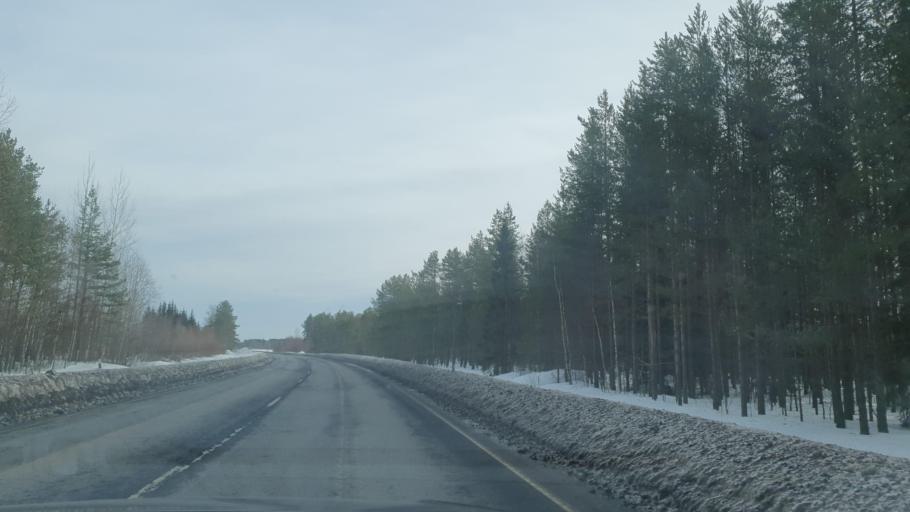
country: FI
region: Northern Ostrobothnia
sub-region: Oulunkaari
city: Utajaervi
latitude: 64.7275
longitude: 26.4880
